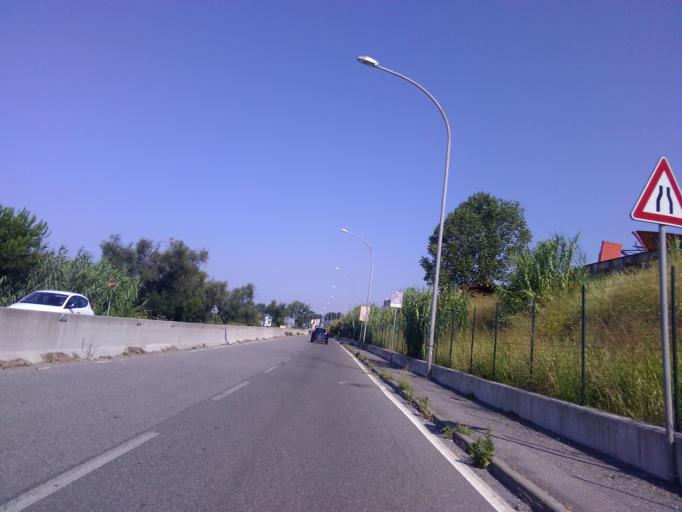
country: IT
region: Tuscany
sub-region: Provincia di Massa-Carrara
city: Massa
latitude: 44.0253
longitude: 10.1004
